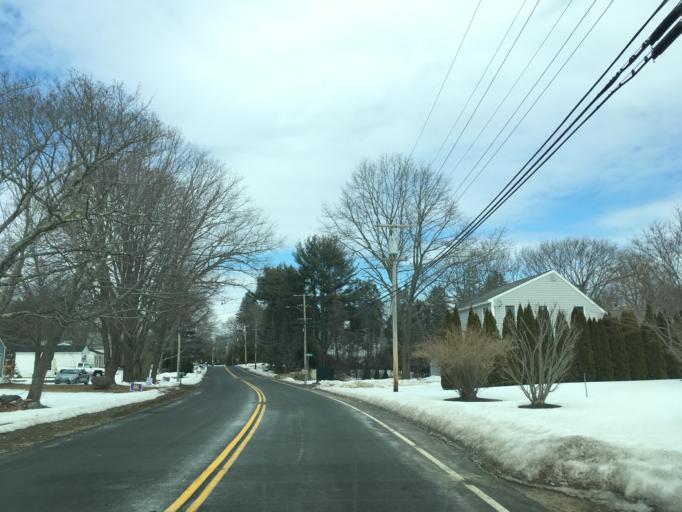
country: US
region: New Hampshire
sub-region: Rockingham County
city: Hampton
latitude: 42.9357
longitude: -70.8192
